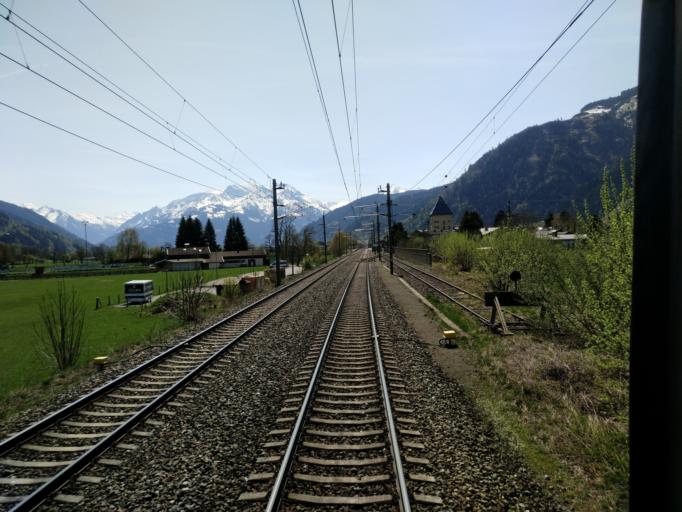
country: AT
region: Salzburg
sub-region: Politischer Bezirk Zell am See
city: Maishofen
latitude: 47.3622
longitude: 12.8123
